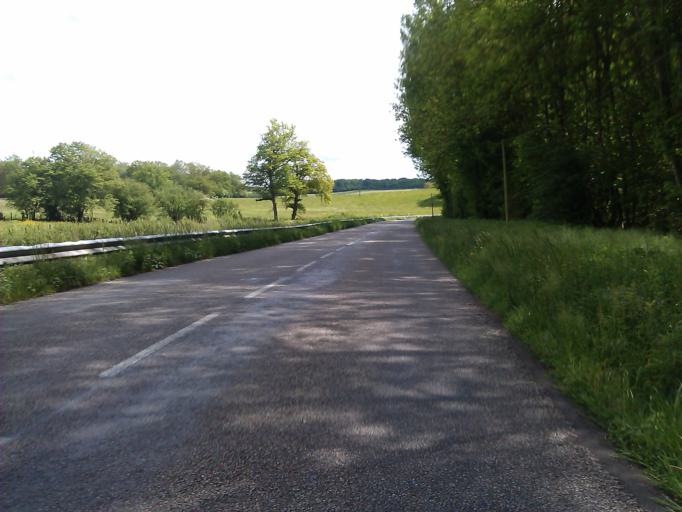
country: FR
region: Bourgogne
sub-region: Departement de Saone-et-Loire
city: Ecuisses
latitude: 46.7882
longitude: 4.5577
